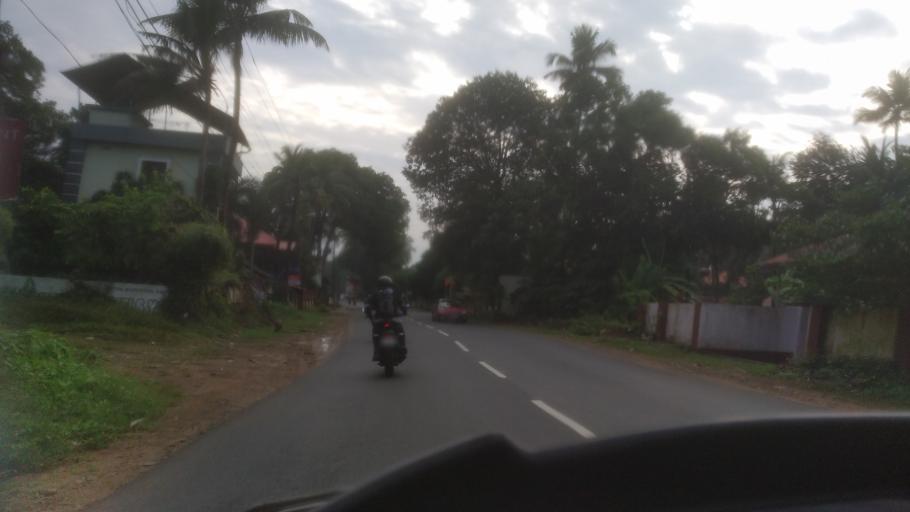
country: IN
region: Kerala
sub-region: Ernakulam
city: Kotamangalam
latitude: 10.0586
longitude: 76.6444
